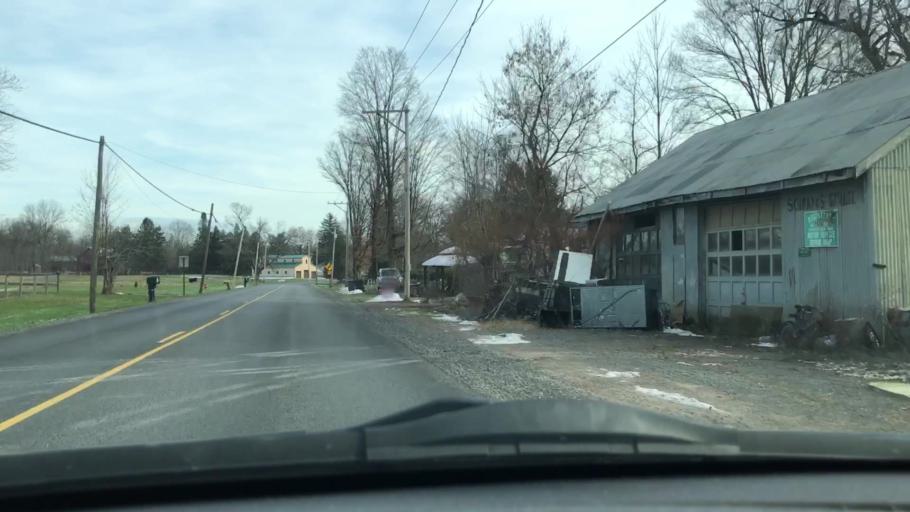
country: US
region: New York
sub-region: Madison County
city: Oneida
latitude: 43.0982
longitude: -75.6316
